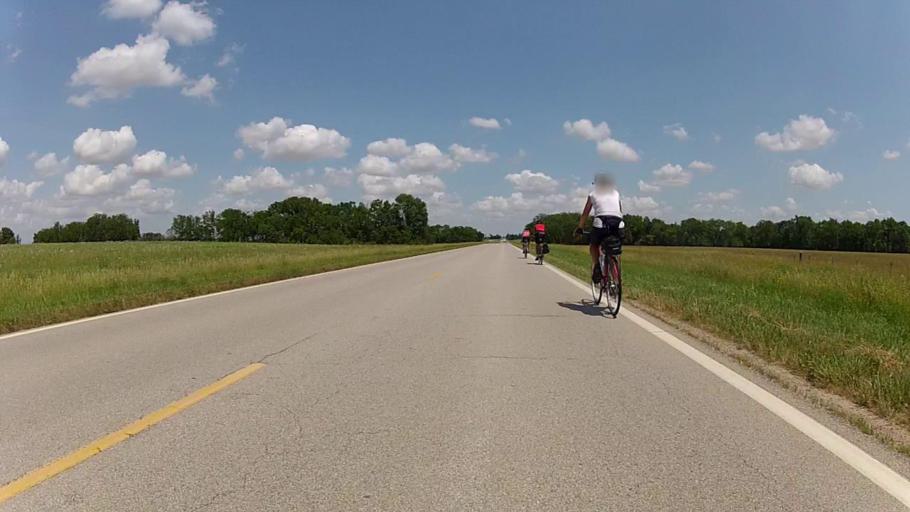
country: US
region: Kansas
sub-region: Labette County
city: Altamont
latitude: 37.1927
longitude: -95.3826
